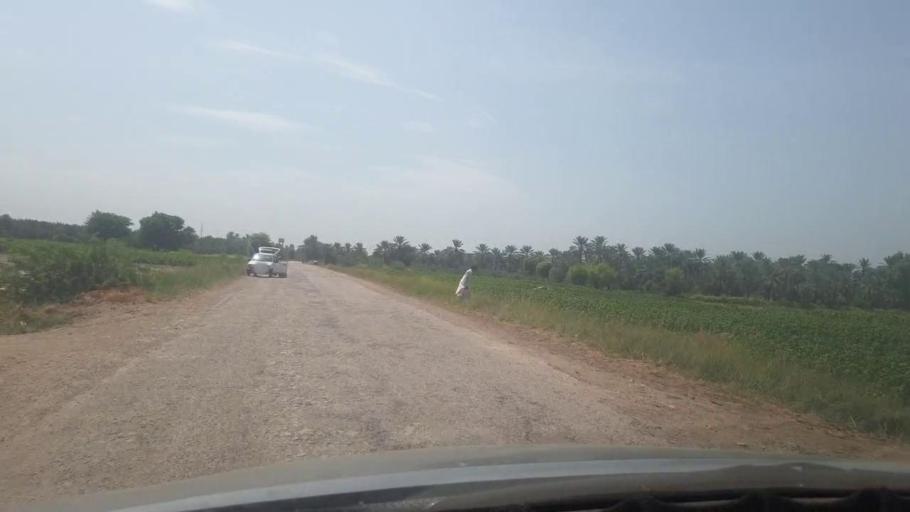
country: PK
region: Sindh
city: Bozdar
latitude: 27.2038
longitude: 68.5815
